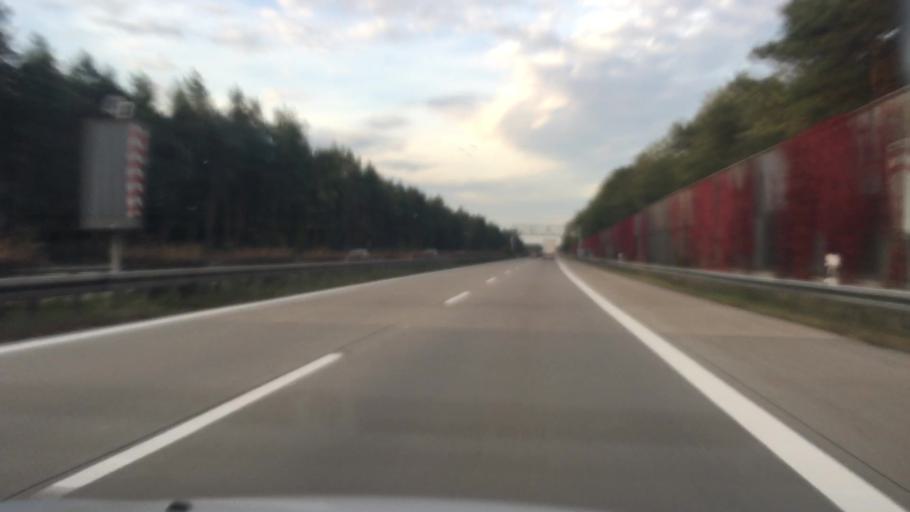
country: DE
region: Brandenburg
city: Ruhland
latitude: 51.4504
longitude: 13.8436
